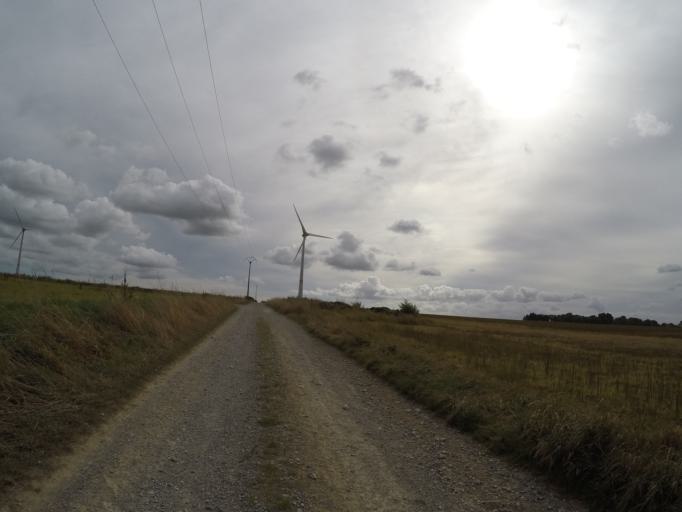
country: BE
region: Wallonia
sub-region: Province de Namur
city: Assesse
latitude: 50.2983
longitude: 4.9824
